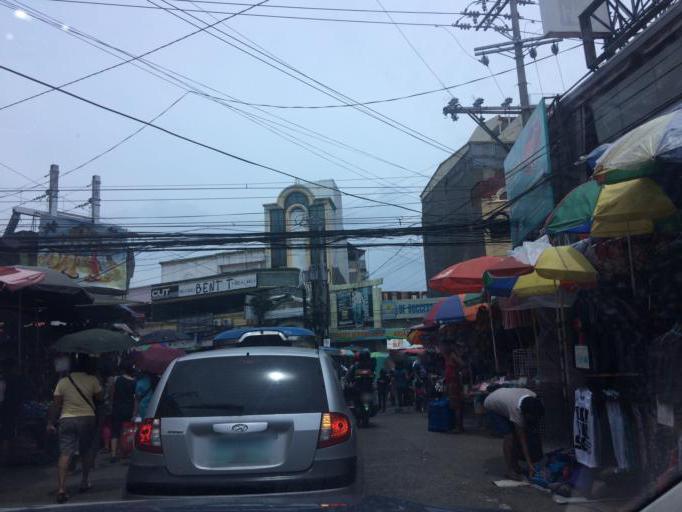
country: PH
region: Metro Manila
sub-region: Makati City
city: Makati City
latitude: 14.5323
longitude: 120.9965
